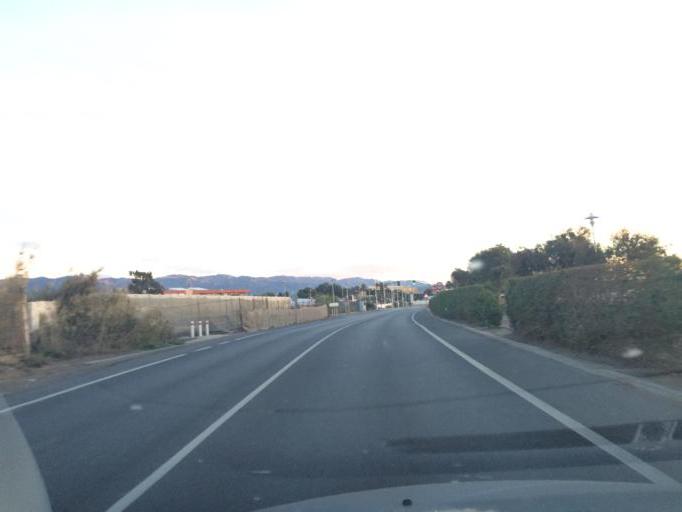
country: ES
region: Andalusia
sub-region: Provincia de Almeria
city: Almeria
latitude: 36.8260
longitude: -2.4060
